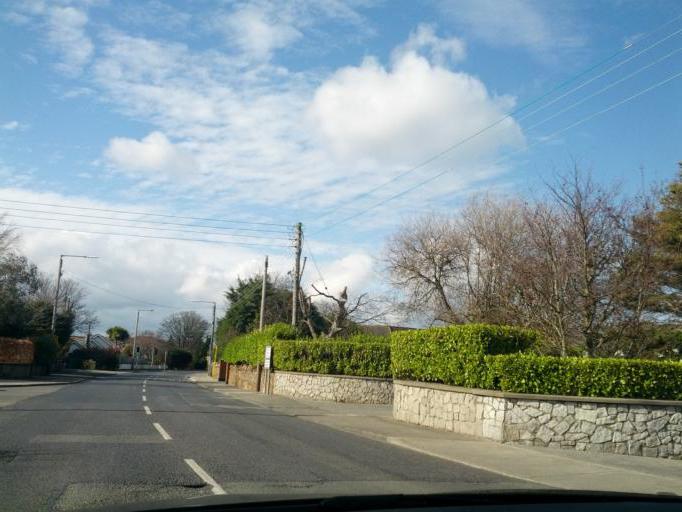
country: IE
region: Leinster
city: Sutton
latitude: 53.3824
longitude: -6.0983
